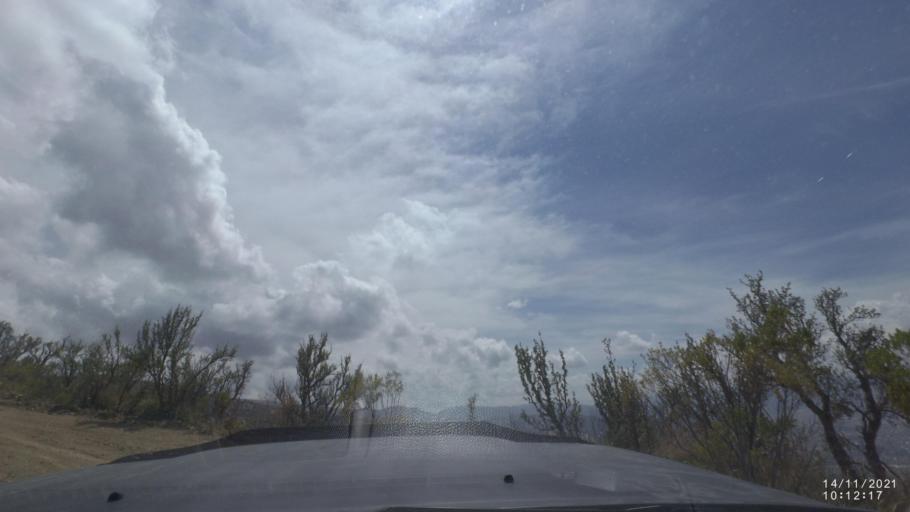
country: BO
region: Cochabamba
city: Cochabamba
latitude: -17.3465
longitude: -66.0862
